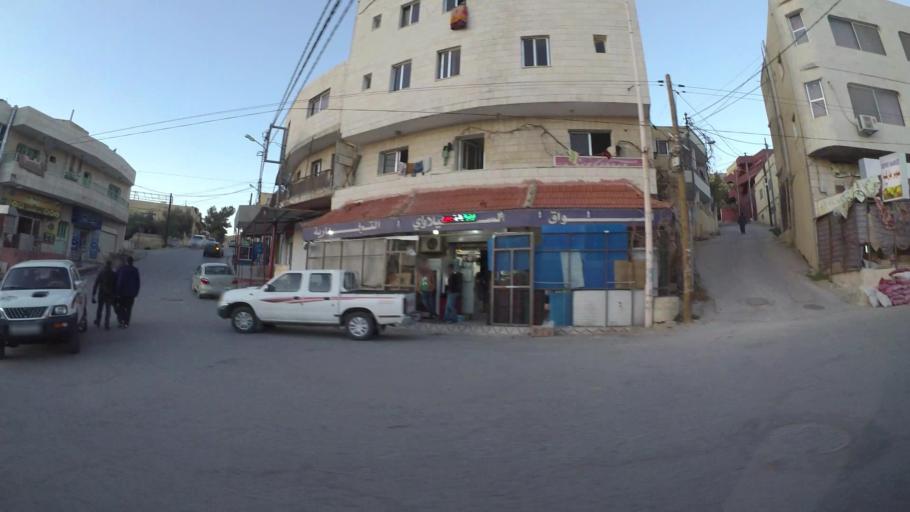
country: JO
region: Ma'an
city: Petra
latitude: 30.3233
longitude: 35.4775
